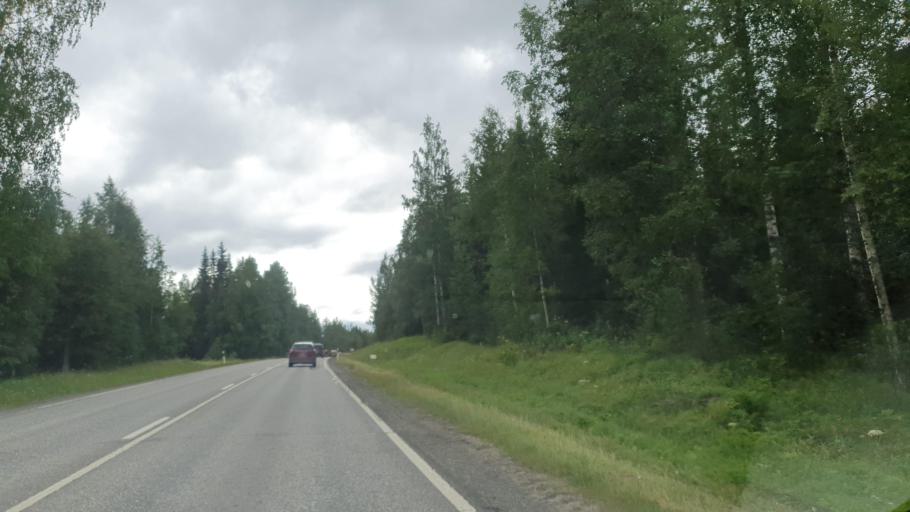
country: FI
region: Northern Savo
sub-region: Ylae-Savo
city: Sonkajaervi
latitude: 63.6865
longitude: 27.3416
